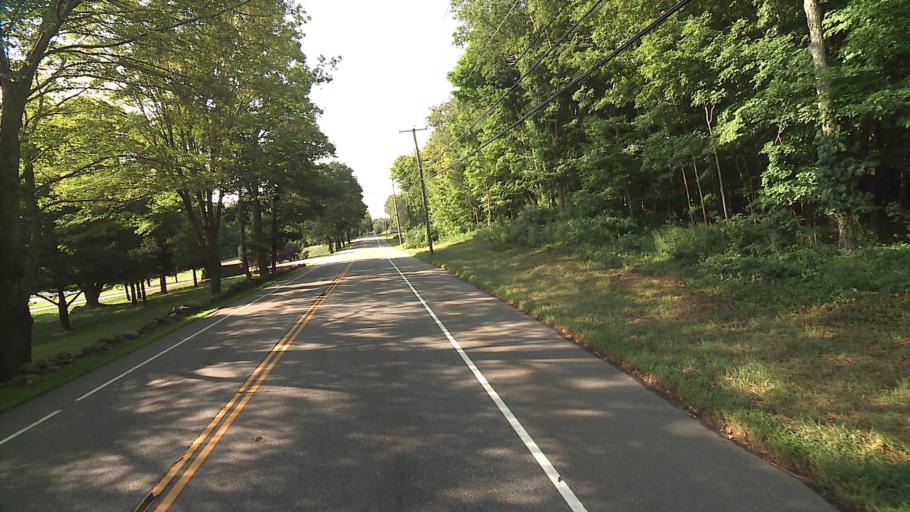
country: US
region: Connecticut
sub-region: New London County
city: Pawcatuck
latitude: 41.4188
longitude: -71.8577
